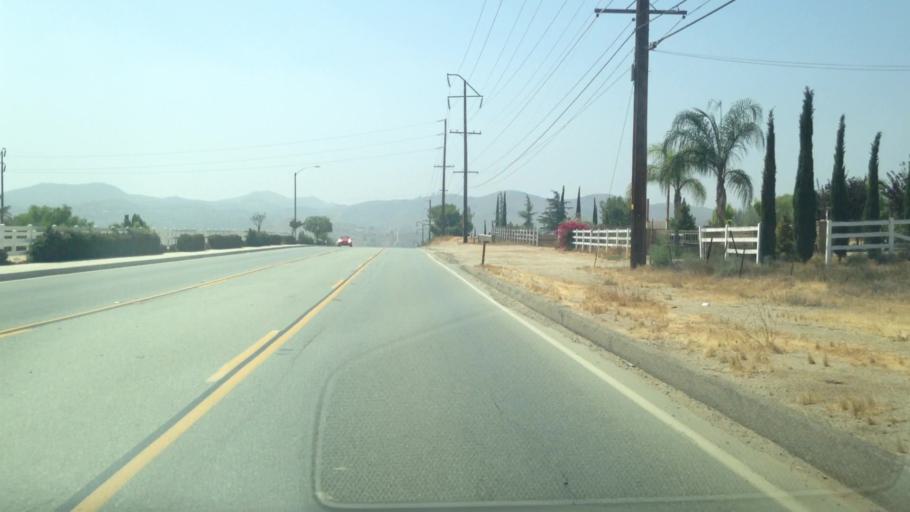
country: US
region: California
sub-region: Riverside County
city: Mead Valley
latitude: 33.8453
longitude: -117.3312
